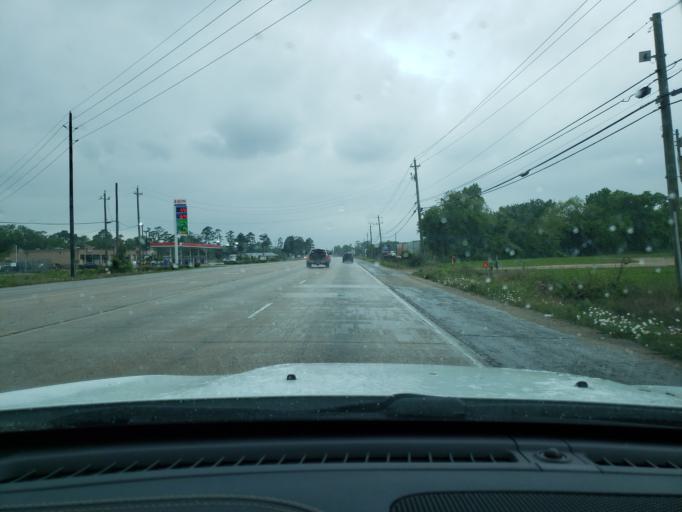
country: US
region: Texas
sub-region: Chambers County
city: Mont Belvieu
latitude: 29.7972
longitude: -94.9066
